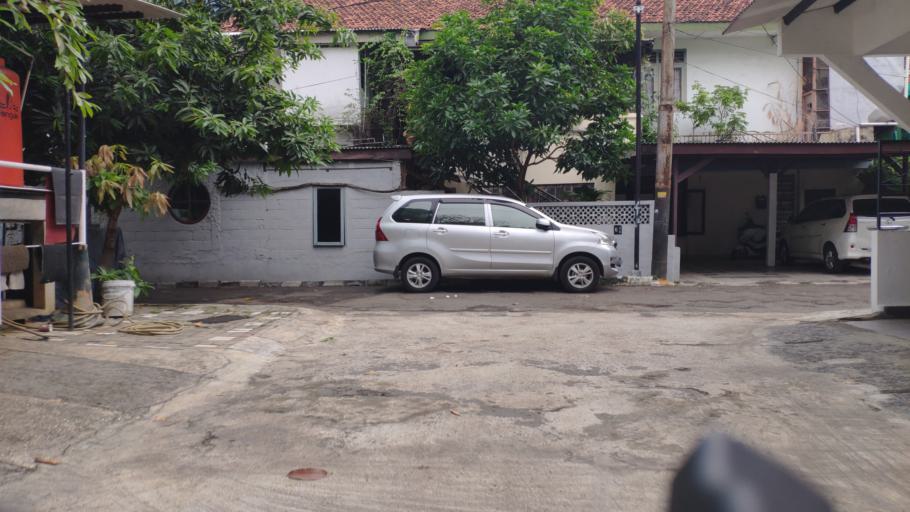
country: ID
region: Jakarta Raya
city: Jakarta
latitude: -6.2203
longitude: 106.8449
